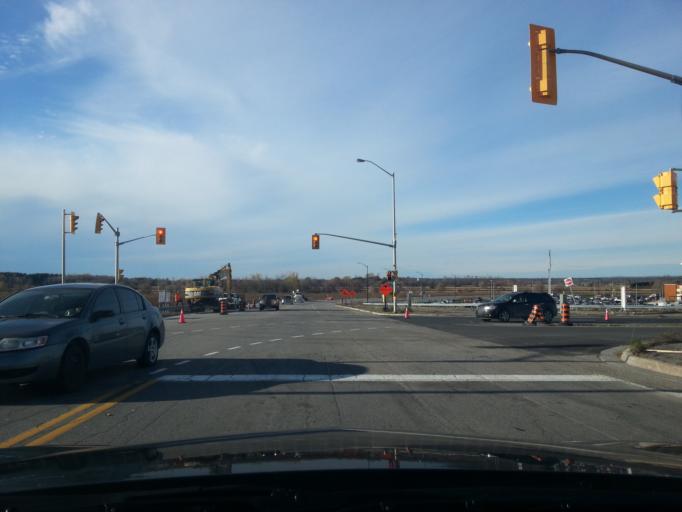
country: CA
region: Ontario
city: Bells Corners
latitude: 45.2947
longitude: -75.9391
